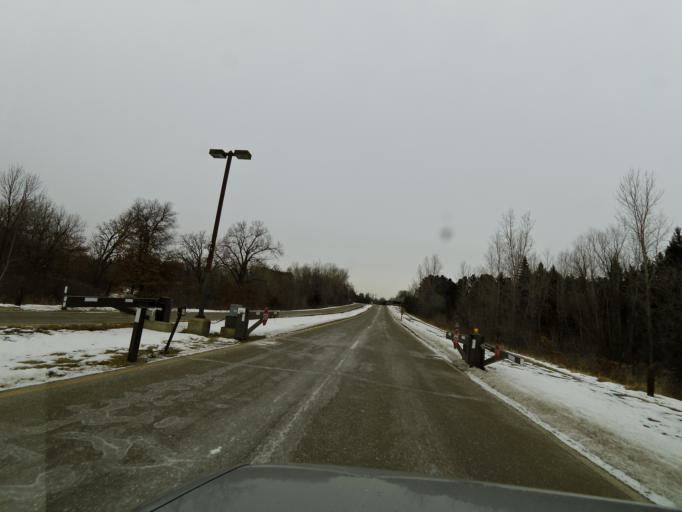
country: US
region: Minnesota
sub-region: Washington County
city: Lake Elmo
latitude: 44.9686
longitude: -92.9033
